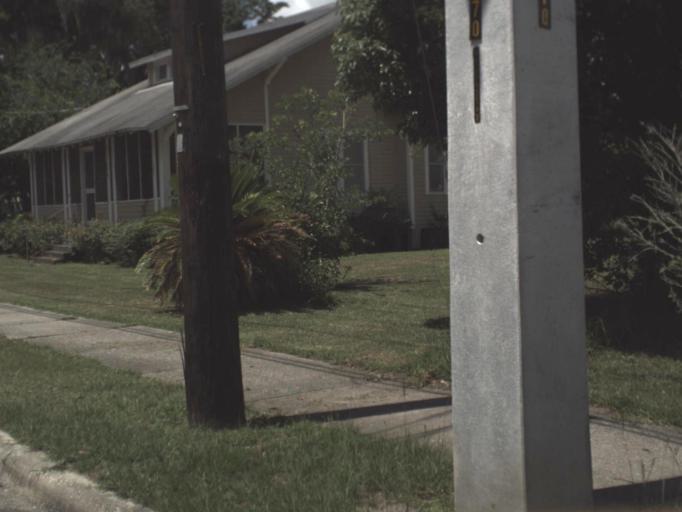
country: US
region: Florida
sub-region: Putnam County
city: Crescent City
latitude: 29.4274
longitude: -81.5104
